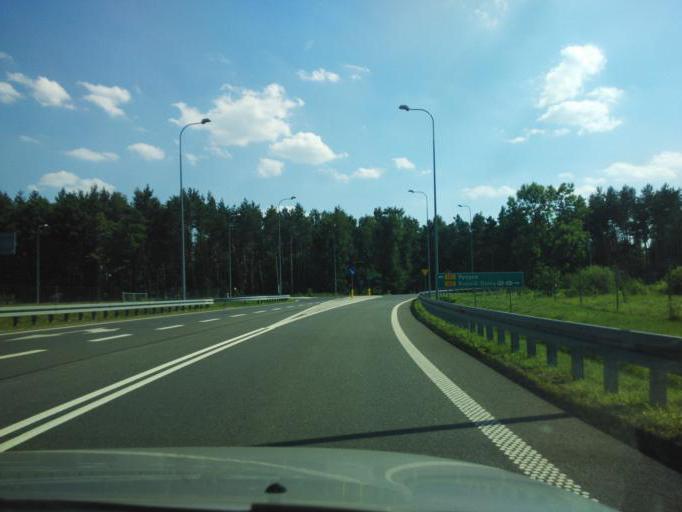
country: PL
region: West Pomeranian Voivodeship
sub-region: Powiat pyrzycki
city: Kozielice
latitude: 53.1208
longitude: 14.7485
